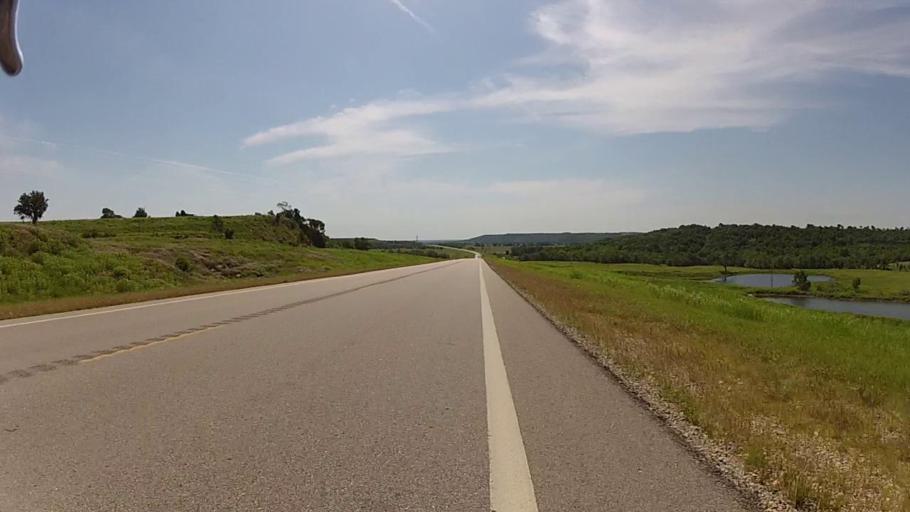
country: US
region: Kansas
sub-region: Chautauqua County
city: Sedan
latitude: 37.1101
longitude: -96.5955
